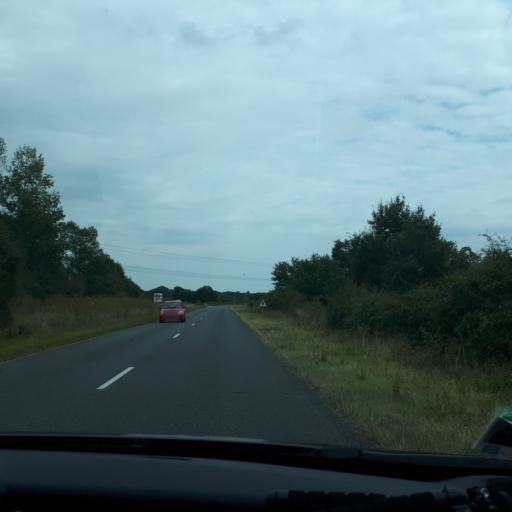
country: FR
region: Centre
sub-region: Departement du Loiret
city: Ouzouer-sur-Loire
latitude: 47.7694
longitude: 2.4480
